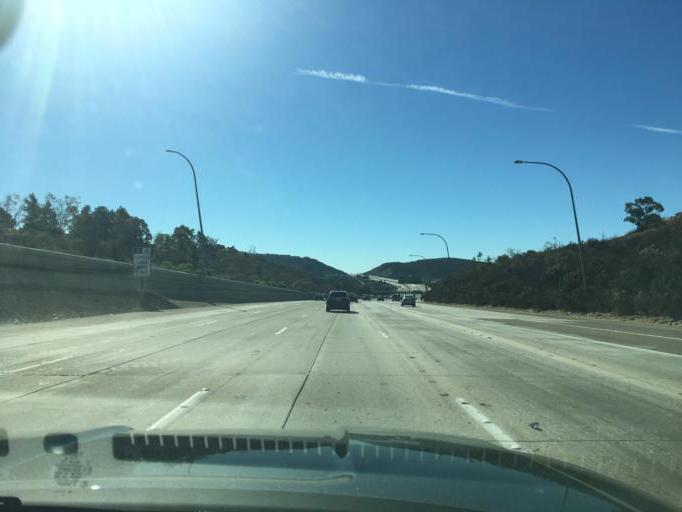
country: US
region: California
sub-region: San Diego County
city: Poway
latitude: 32.9565
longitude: -117.1011
